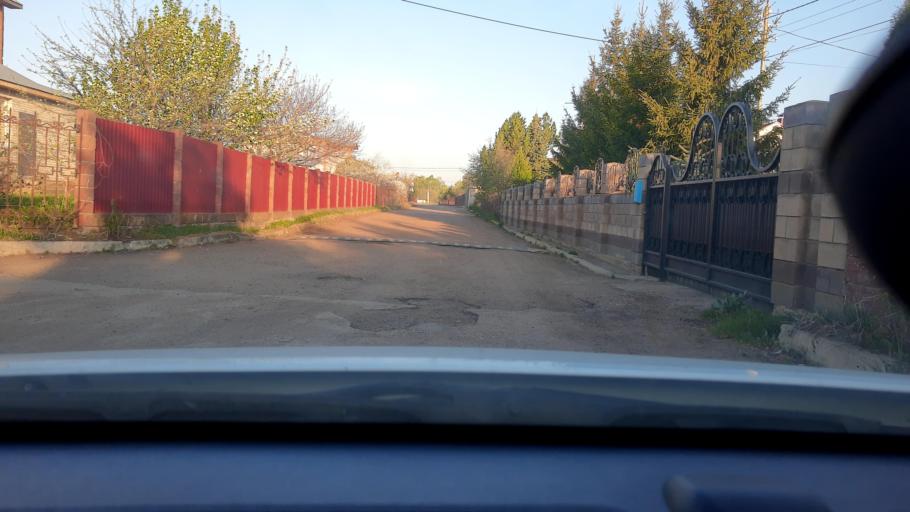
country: RU
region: Bashkortostan
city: Avdon
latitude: 54.5055
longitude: 55.8192
